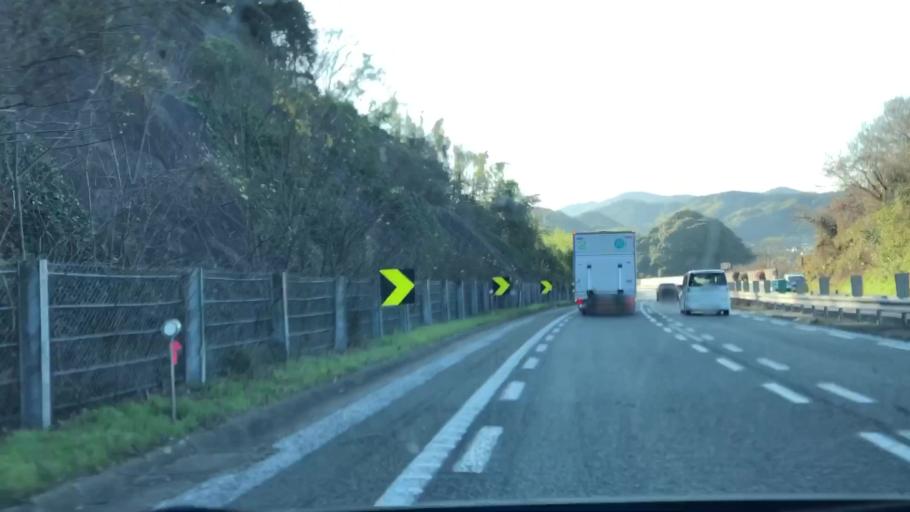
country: JP
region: Yamaguchi
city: Onoda
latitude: 34.1100
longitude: 131.1549
